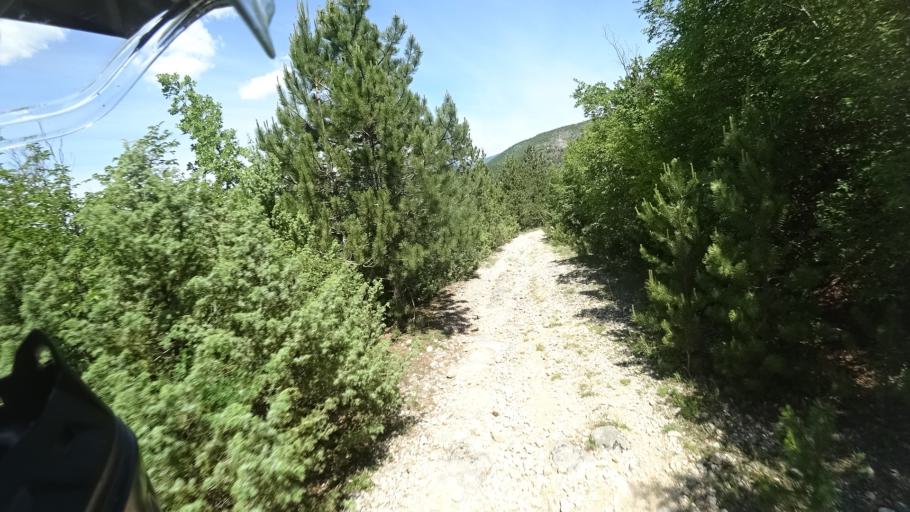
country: HR
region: Sibensko-Kniniska
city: Knin
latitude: 44.0351
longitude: 16.2296
